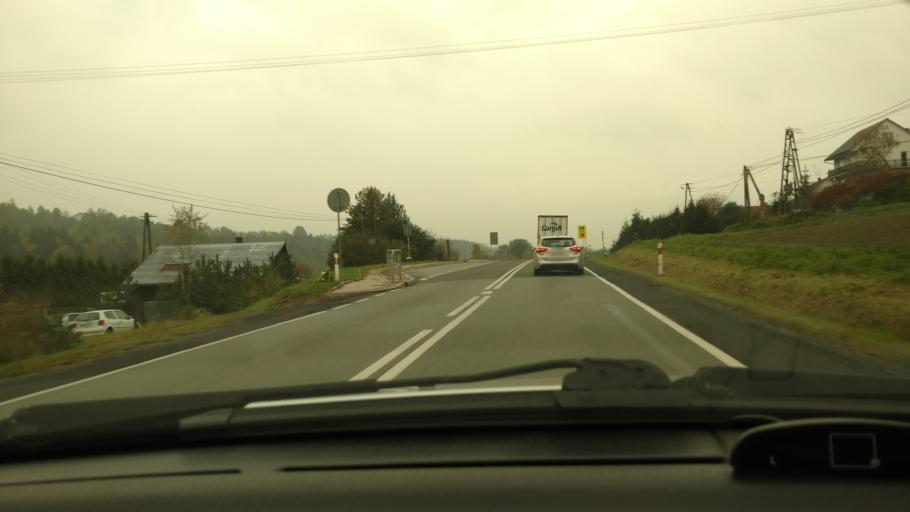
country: PL
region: Lesser Poland Voivodeship
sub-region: Powiat nowosadecki
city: Kamionka Wielka
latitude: 49.6151
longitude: 20.8141
